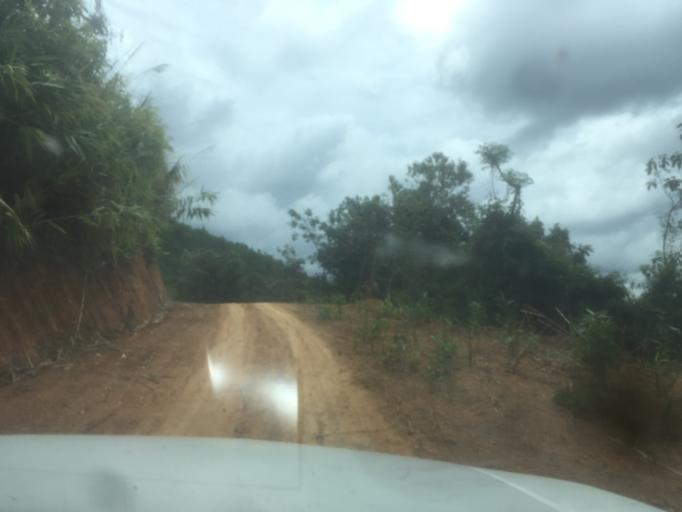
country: LA
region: Phongsali
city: Khoa
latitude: 20.9265
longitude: 102.5357
